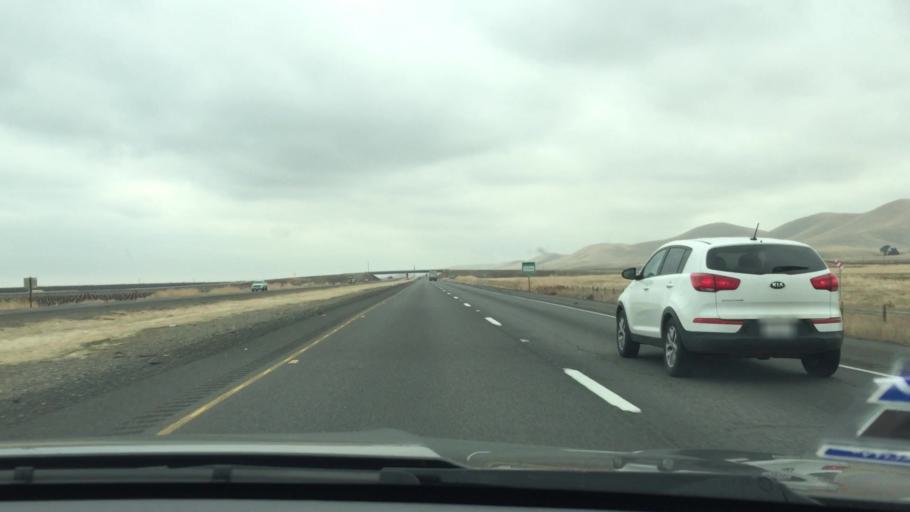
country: US
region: California
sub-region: Merced County
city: Gustine
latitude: 37.2244
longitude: -121.0835
